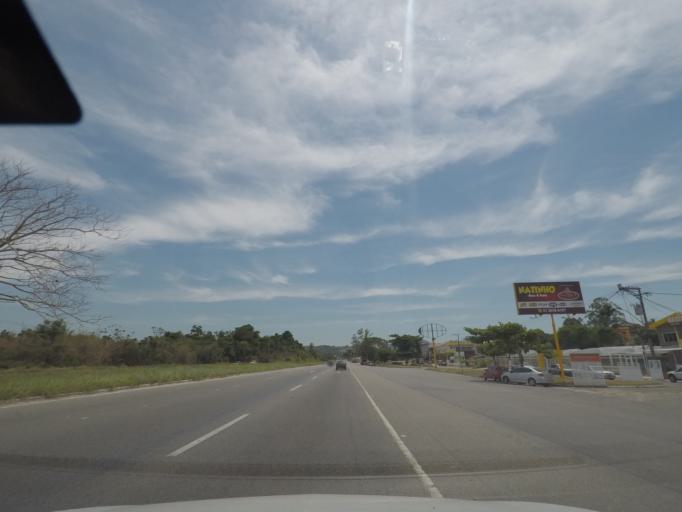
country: BR
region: Rio de Janeiro
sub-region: Marica
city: Marica
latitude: -22.9137
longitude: -42.8457
